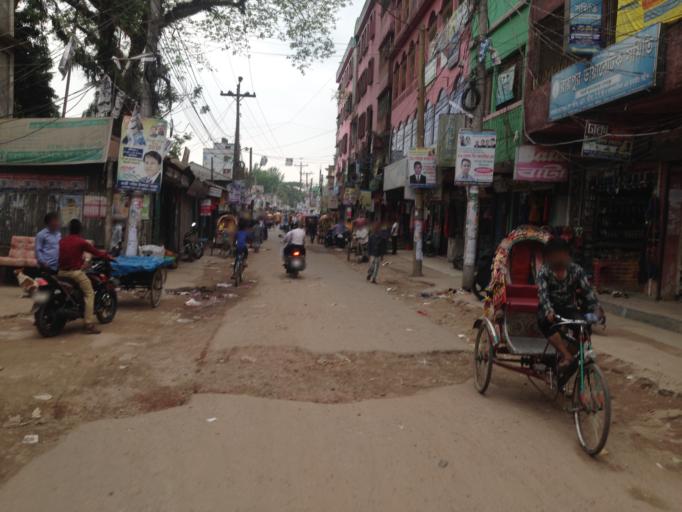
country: BD
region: Chittagong
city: Raipur
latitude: 23.0366
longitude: 90.7667
